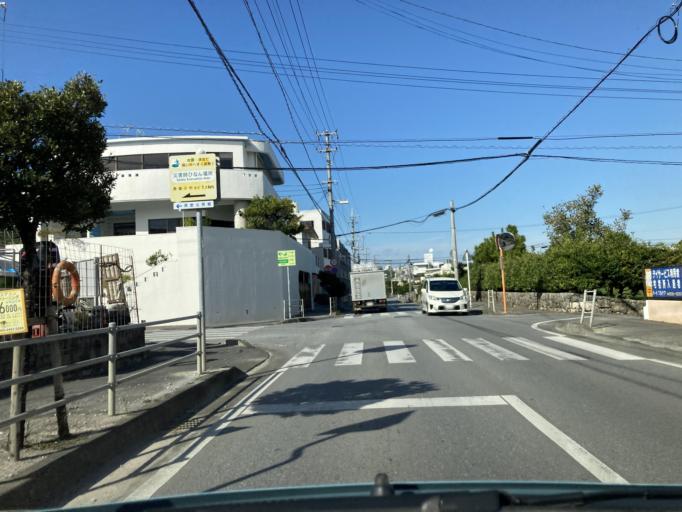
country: JP
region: Okinawa
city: Tomigusuku
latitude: 26.1816
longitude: 127.7068
